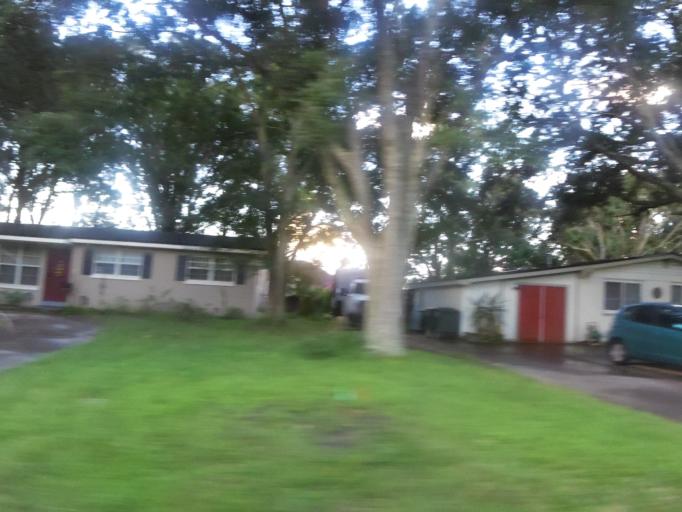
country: US
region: Florida
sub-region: Duval County
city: Jacksonville
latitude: 30.2324
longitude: -81.6113
